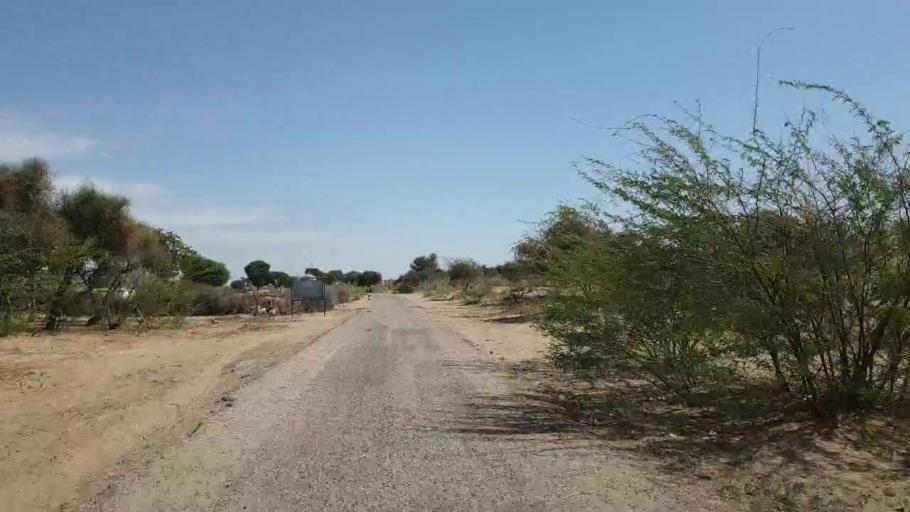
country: PK
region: Sindh
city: Umarkot
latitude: 25.1645
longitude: 69.9960
